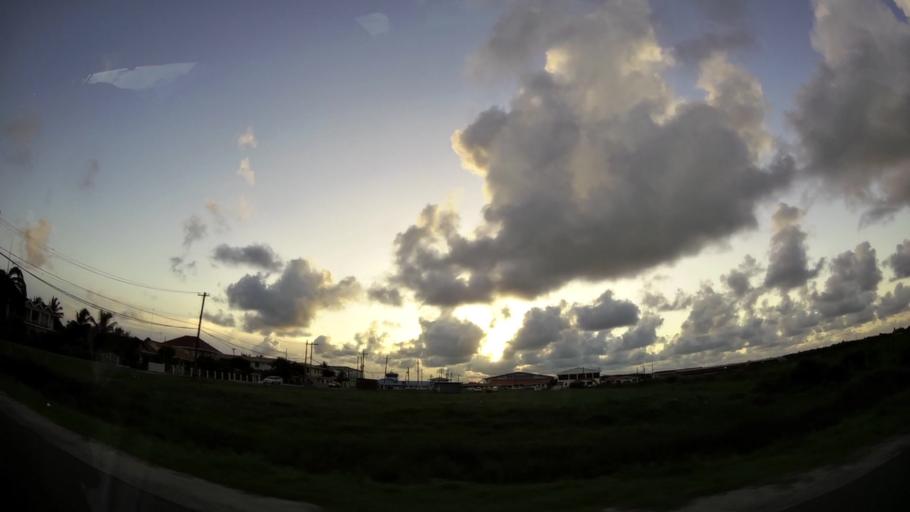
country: GY
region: Demerara-Mahaica
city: Georgetown
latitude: 6.8068
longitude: -58.1011
